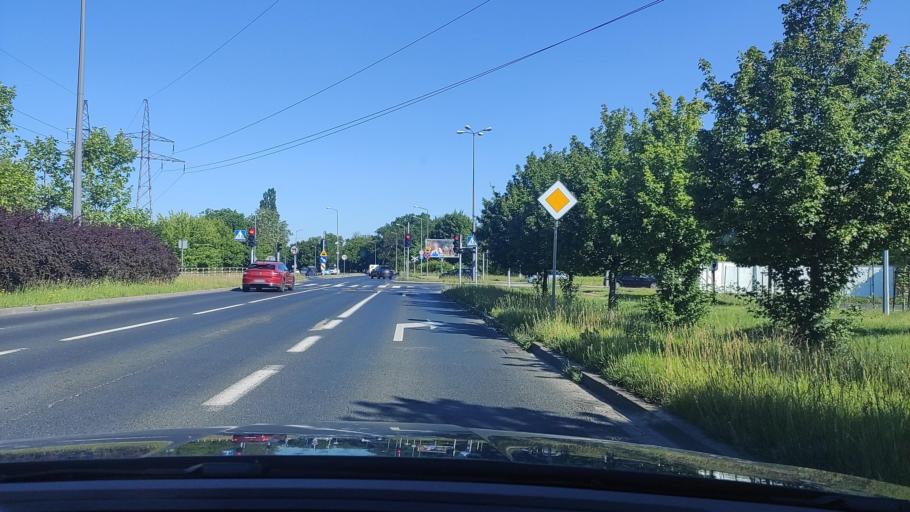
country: PL
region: Greater Poland Voivodeship
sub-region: Poznan
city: Poznan
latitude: 52.3933
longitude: 16.9913
